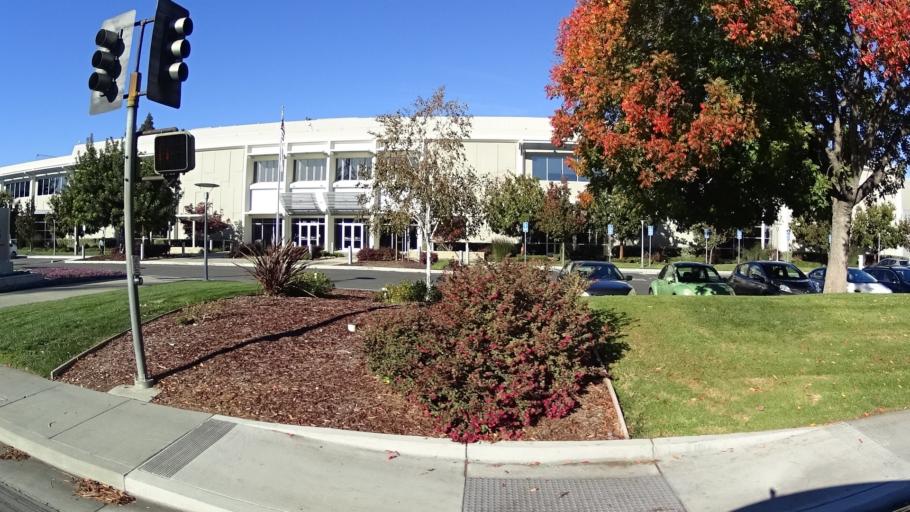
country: US
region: California
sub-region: Santa Clara County
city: Sunnyvale
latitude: 37.3739
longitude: -122.0016
